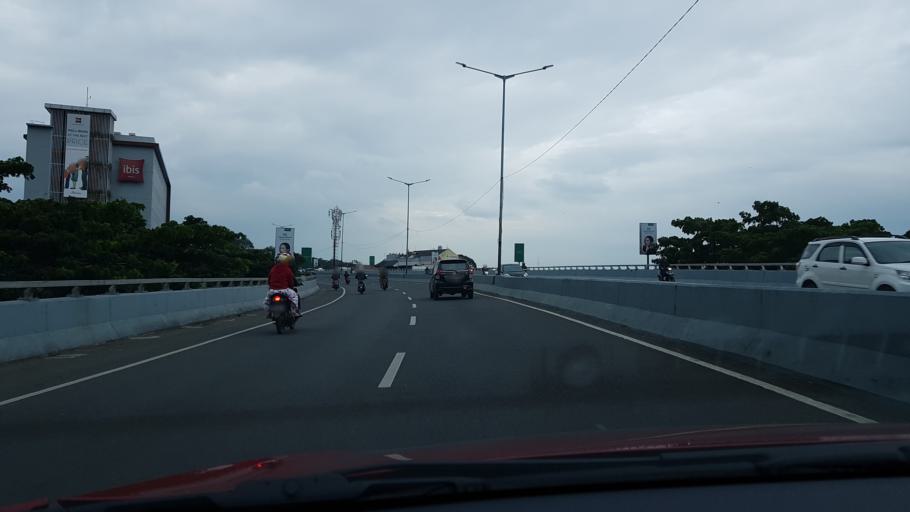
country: ID
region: West Java
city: Bandung
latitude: -6.8995
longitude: 107.5949
